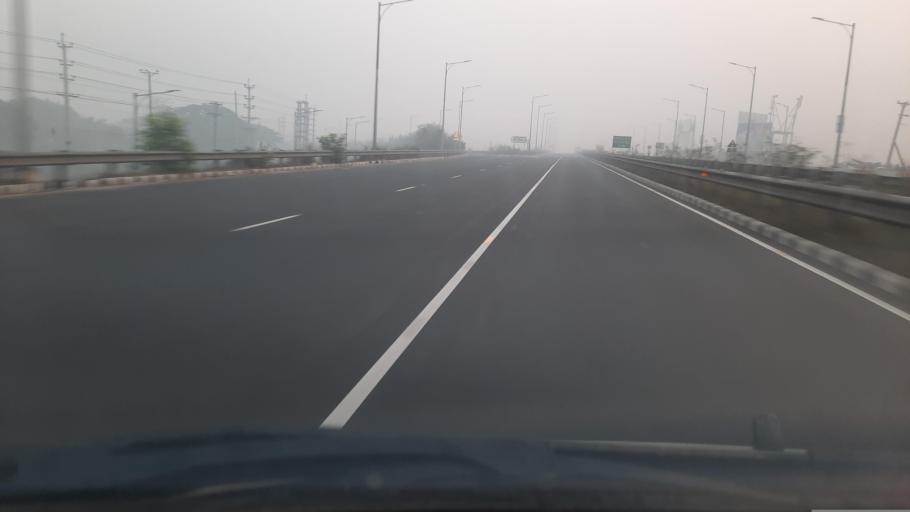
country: BD
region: Dhaka
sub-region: Dhaka
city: Dhaka
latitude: 23.6732
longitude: 90.4027
